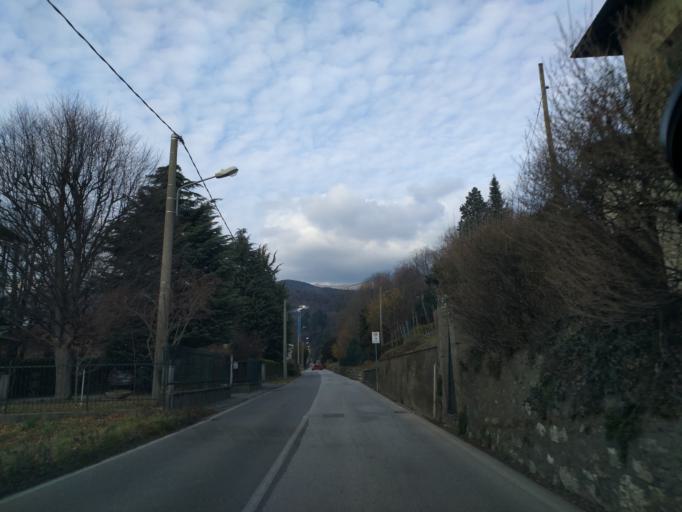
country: IT
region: Lombardy
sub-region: Provincia di Como
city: Albese Con Cassano
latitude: 45.7915
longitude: 9.1595
